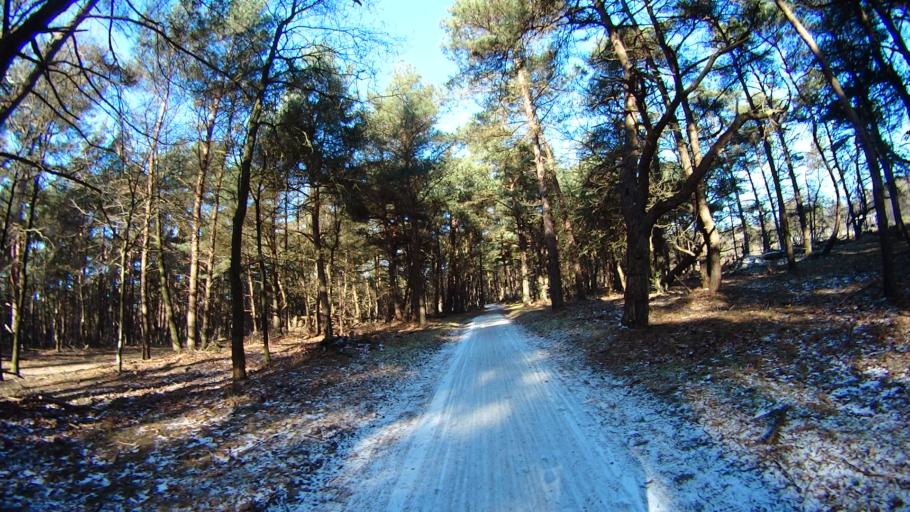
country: NL
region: North Holland
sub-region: Gemeente Laren
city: Laren
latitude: 52.2567
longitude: 5.2024
